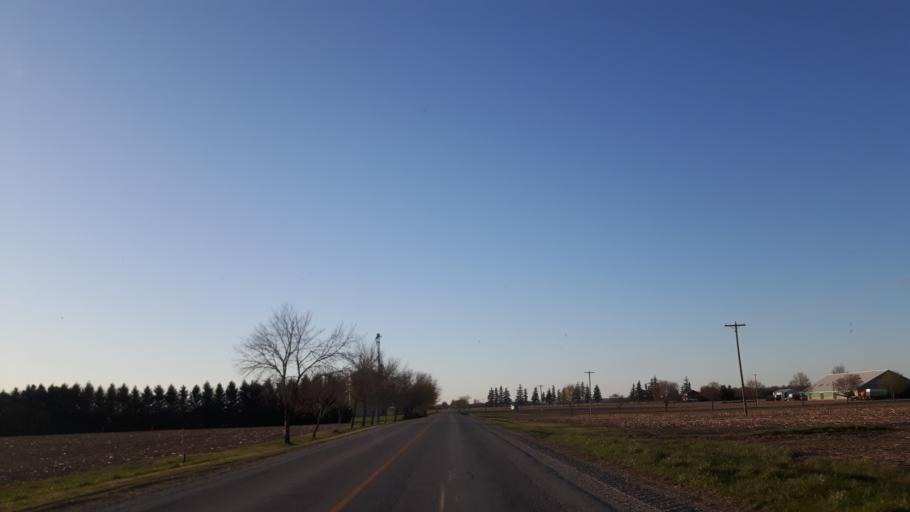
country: CA
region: Ontario
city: Bluewater
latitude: 43.5481
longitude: -81.5476
